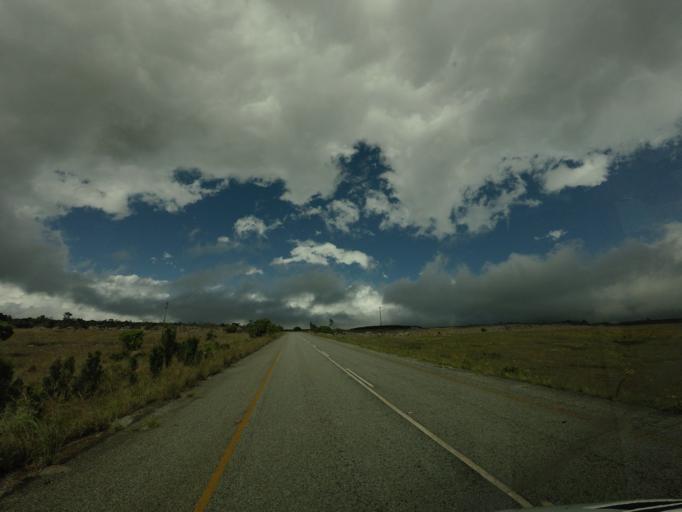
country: ZA
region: Mpumalanga
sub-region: Ehlanzeni District
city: Graksop
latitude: -24.8627
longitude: 30.8608
